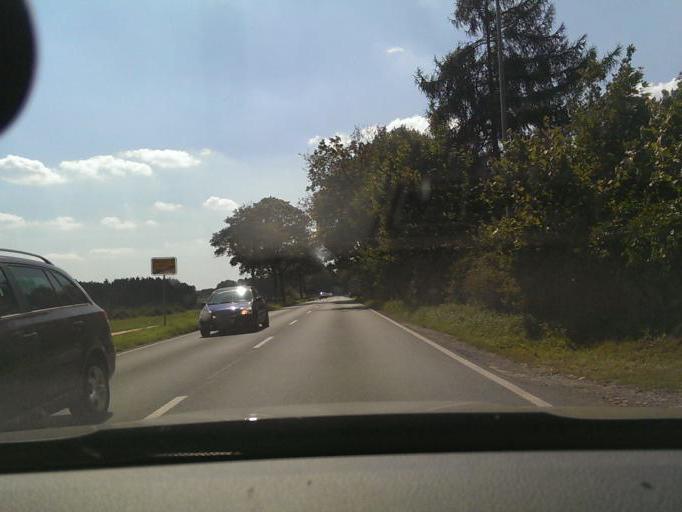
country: DE
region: Lower Saxony
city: Elze
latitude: 52.5611
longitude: 9.7248
